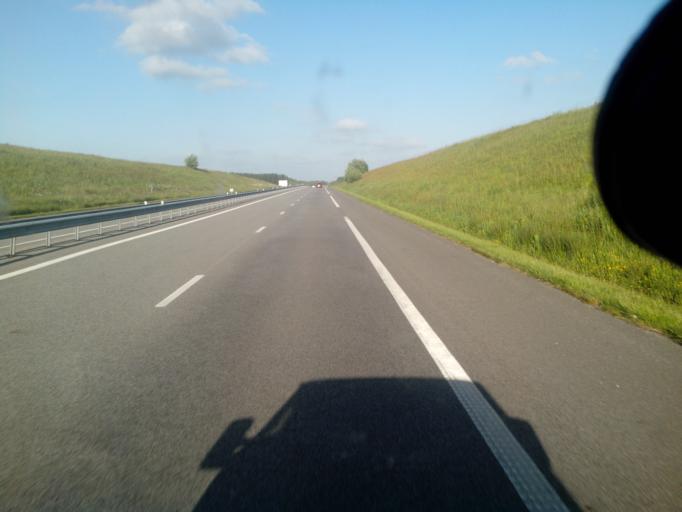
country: FR
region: Haute-Normandie
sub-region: Departement de la Seine-Maritime
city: Limesy
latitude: 49.6441
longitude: 0.9835
